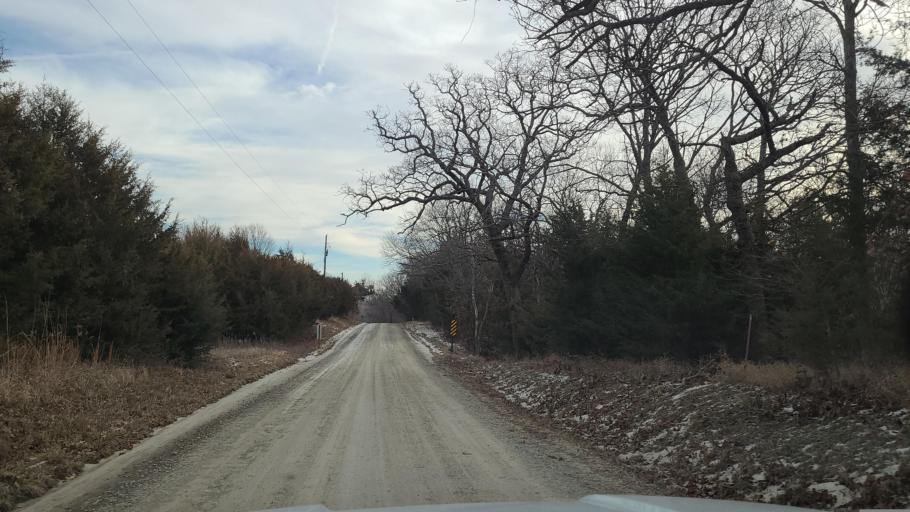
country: US
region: Kansas
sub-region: Douglas County
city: Lawrence
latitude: 39.0368
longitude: -95.3748
